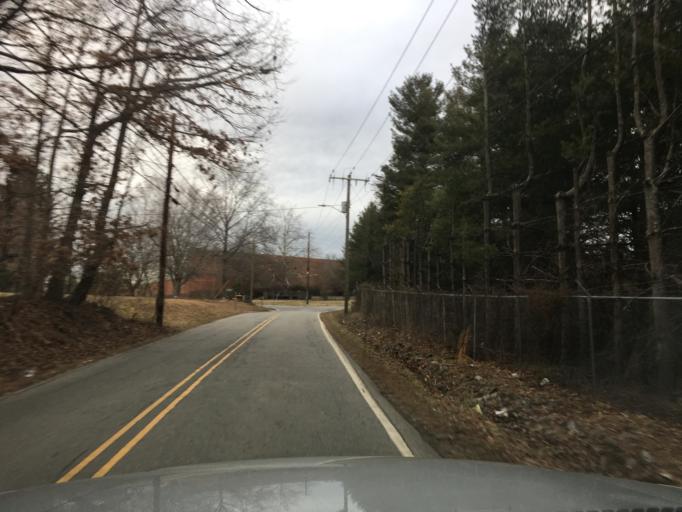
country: US
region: North Carolina
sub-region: Buncombe County
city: Woodfin
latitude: 35.6031
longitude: -82.5864
